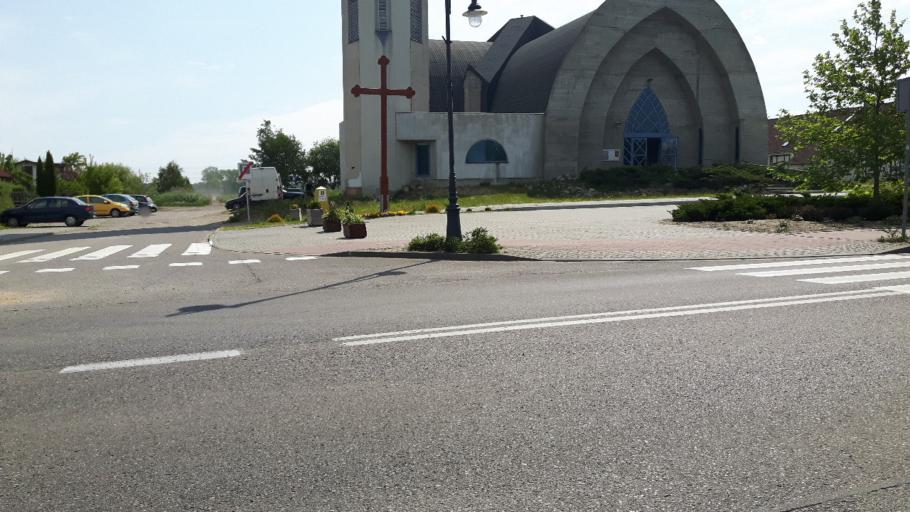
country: PL
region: Pomeranian Voivodeship
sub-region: Powiat leborski
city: Leba
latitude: 54.7559
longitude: 17.5627
